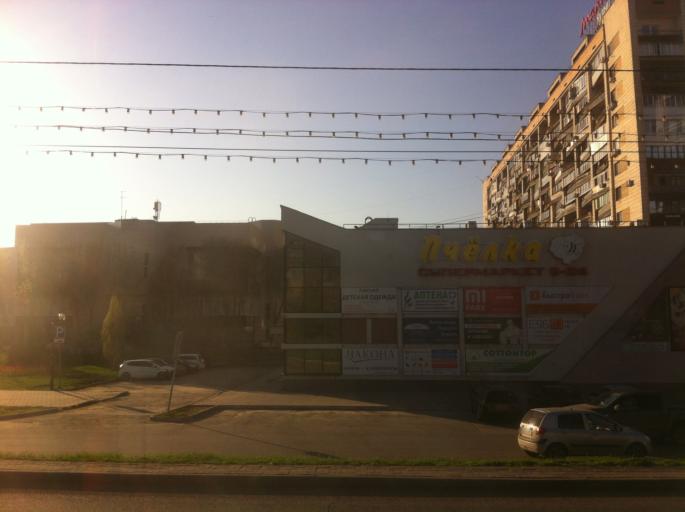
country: RU
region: Samara
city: Samara
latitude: 53.2090
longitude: 50.1376
